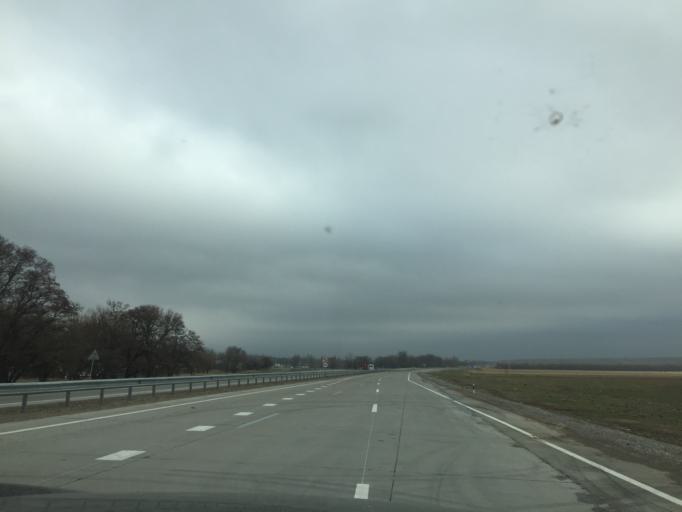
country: KZ
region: Ongtustik Qazaqstan
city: Kokterek
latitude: 42.5547
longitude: 70.1420
